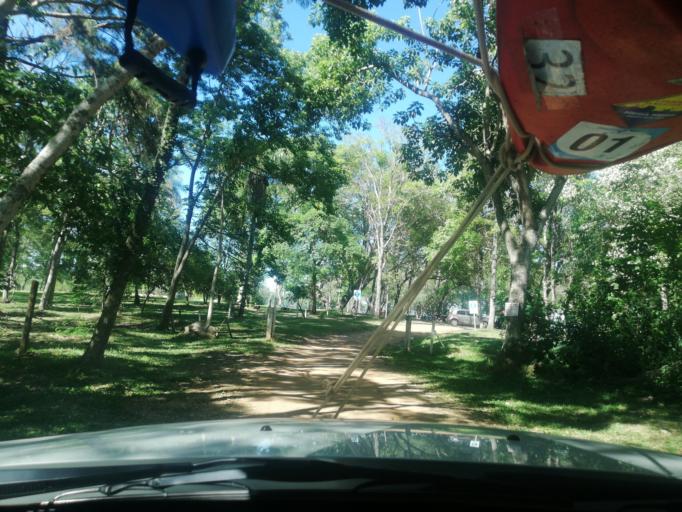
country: AR
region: Misiones
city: Santa Ana
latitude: -27.3306
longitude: -55.5864
